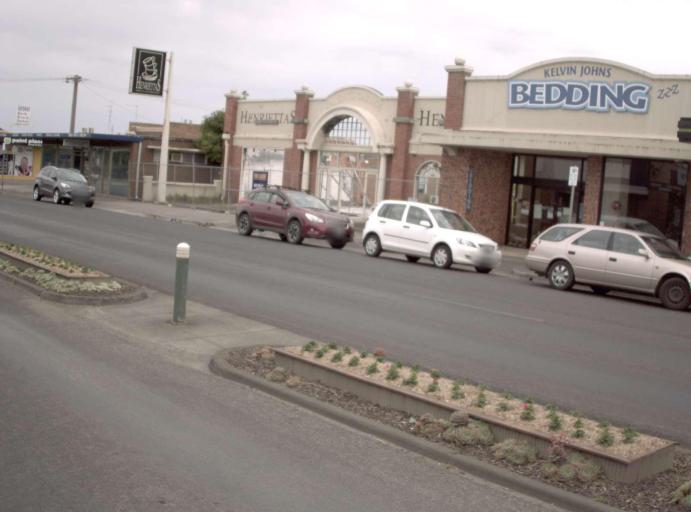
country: AU
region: Victoria
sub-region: Baw Baw
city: Warragul
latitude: -38.4779
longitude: 145.9470
